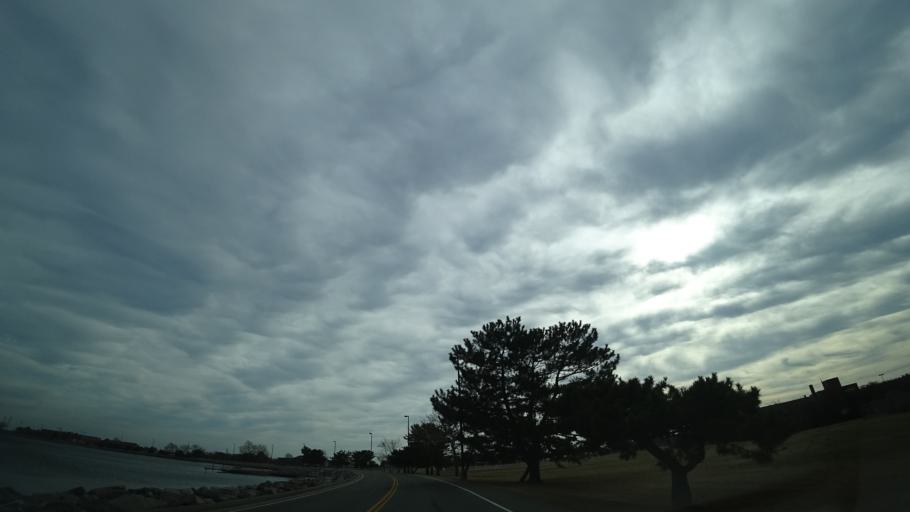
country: US
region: Virginia
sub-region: City of Hampton
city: East Hampton
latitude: 37.0092
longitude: -76.3089
